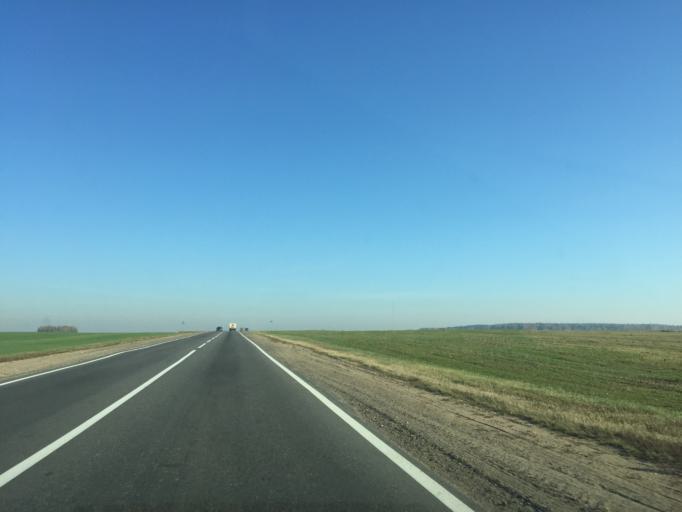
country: BY
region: Mogilev
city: Buynichy
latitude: 53.9600
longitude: 30.2411
